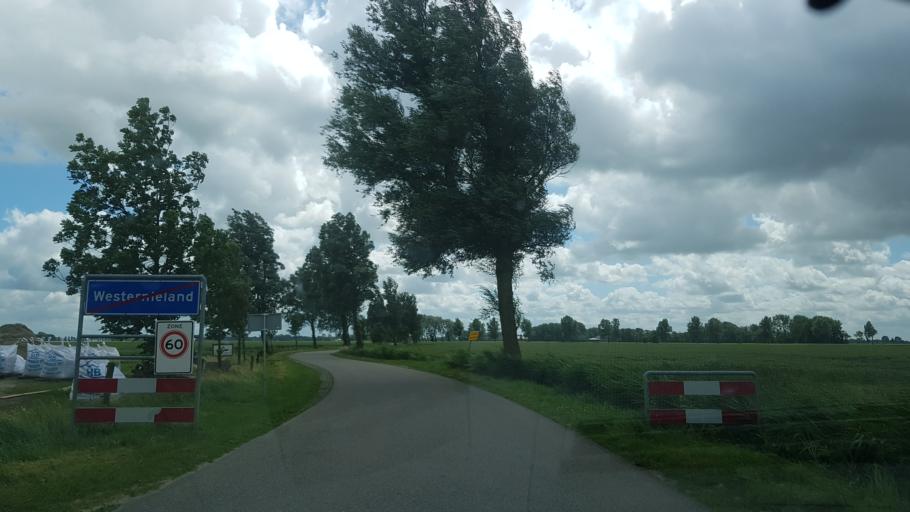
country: NL
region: Groningen
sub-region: Gemeente Winsum
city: Winsum
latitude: 53.3994
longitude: 6.4760
